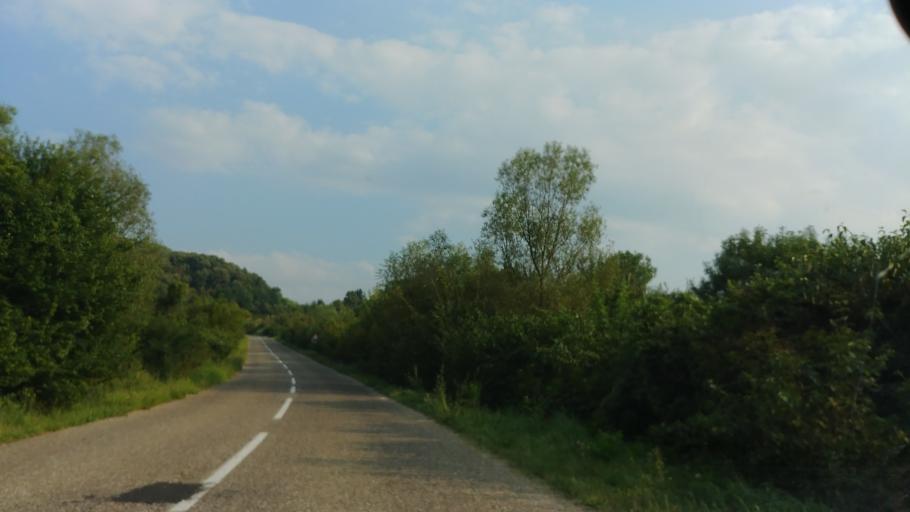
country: BA
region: Republika Srpska
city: Lopare
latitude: 44.7388
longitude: 18.8771
